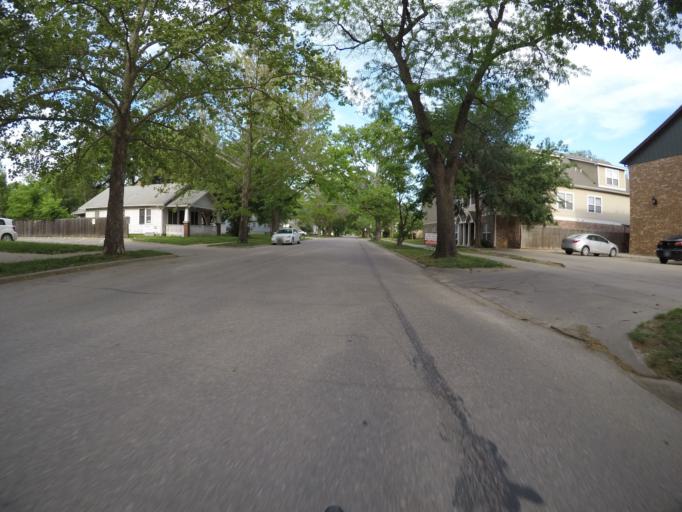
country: US
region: Kansas
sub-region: Riley County
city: Manhattan
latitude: 39.1909
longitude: -96.5739
